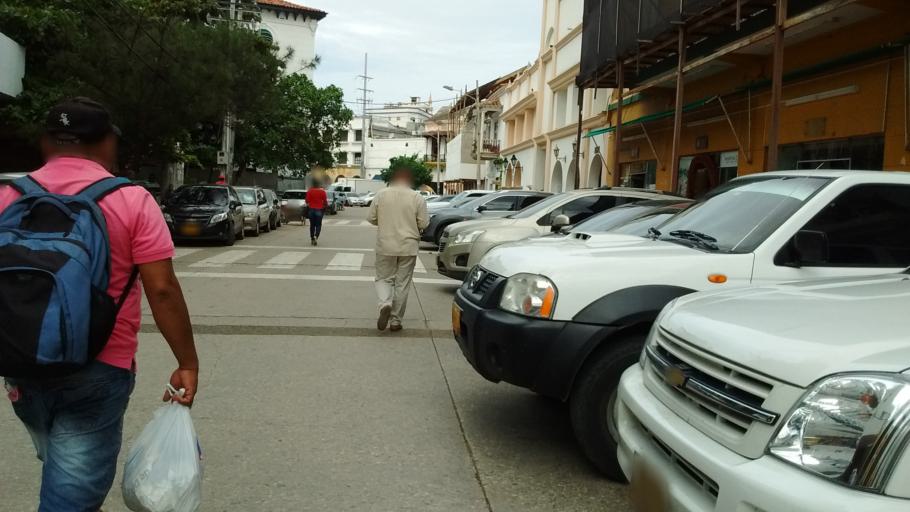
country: CO
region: Bolivar
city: Cartagena
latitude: 10.4248
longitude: -75.5475
